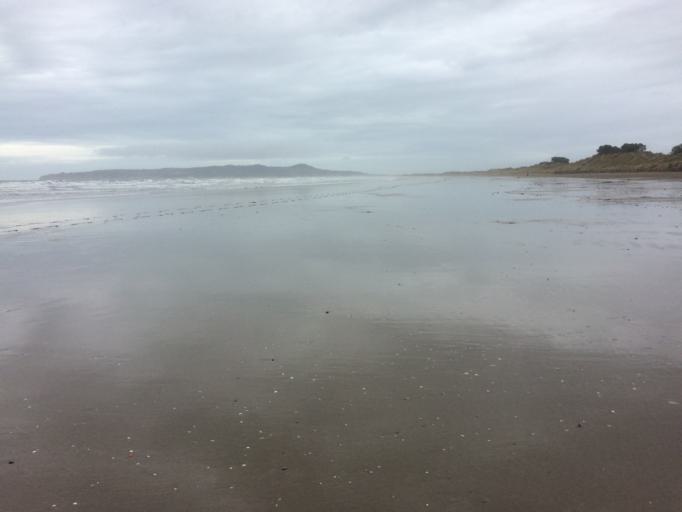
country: IE
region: Leinster
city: Portmarnock
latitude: 53.4300
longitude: -6.1234
